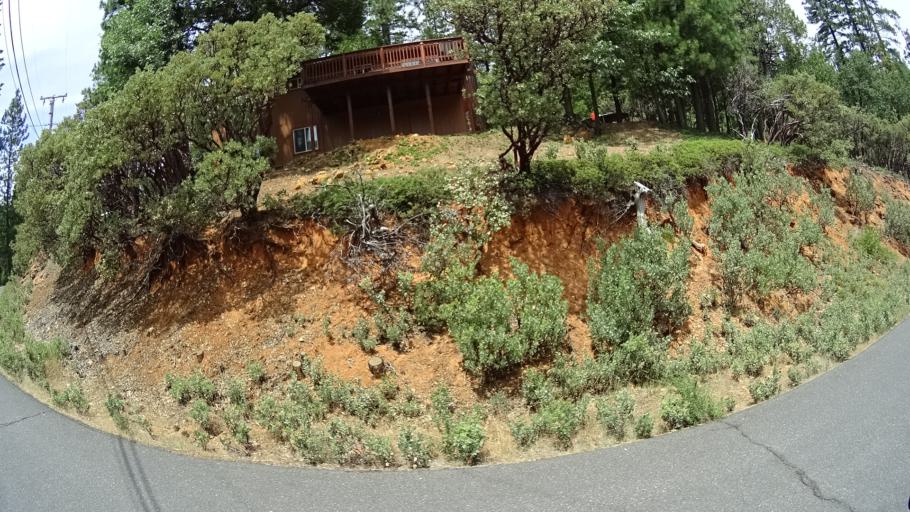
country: US
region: California
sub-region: Calaveras County
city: Arnold
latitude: 38.2442
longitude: -120.3496
